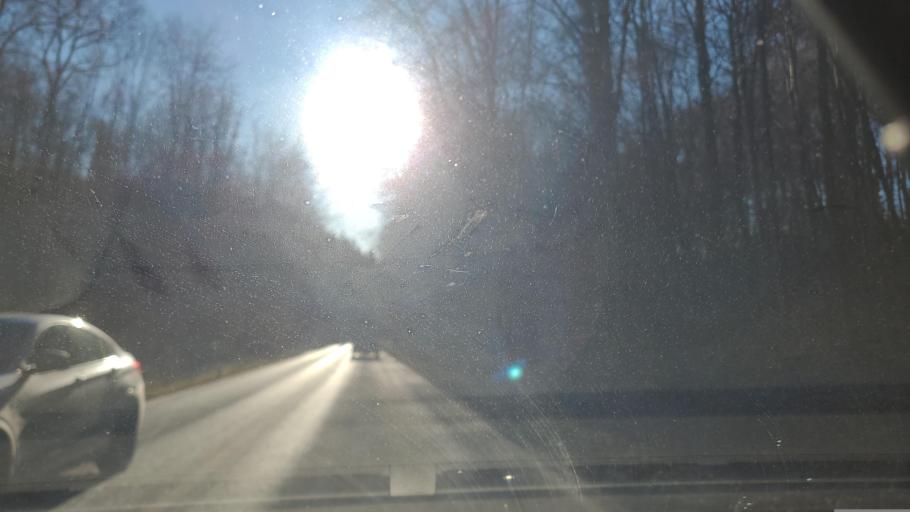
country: LU
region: Luxembourg
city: Bridel
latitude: 49.6383
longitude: 6.0858
